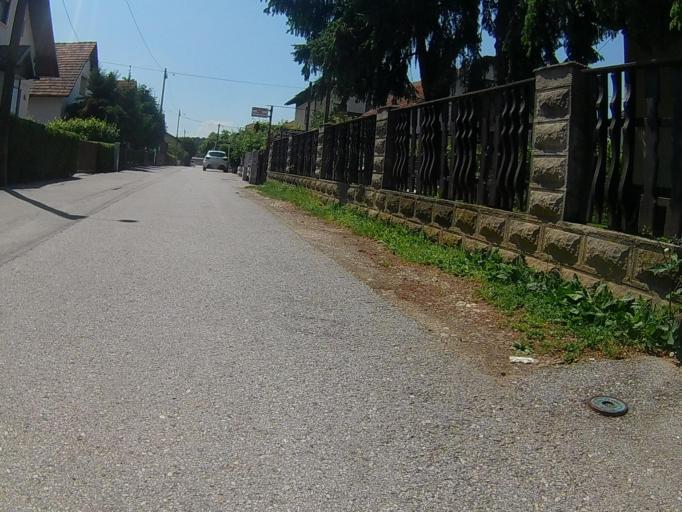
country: SI
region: Hoce-Slivnica
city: Rogoza
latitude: 46.5280
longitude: 15.6783
